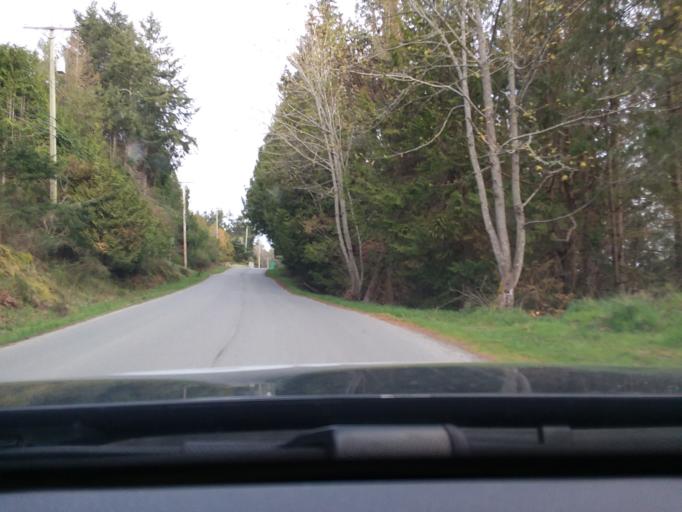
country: CA
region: British Columbia
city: North Saanich
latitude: 48.8752
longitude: -123.3208
